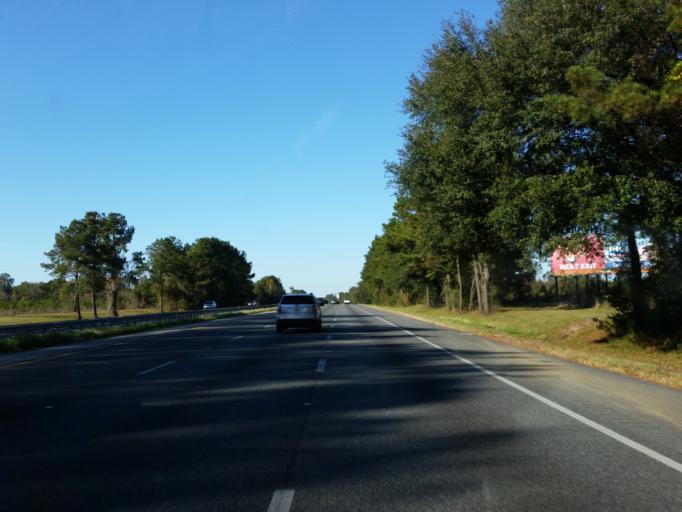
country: US
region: Florida
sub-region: Alachua County
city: High Springs
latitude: 29.9556
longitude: -82.5699
